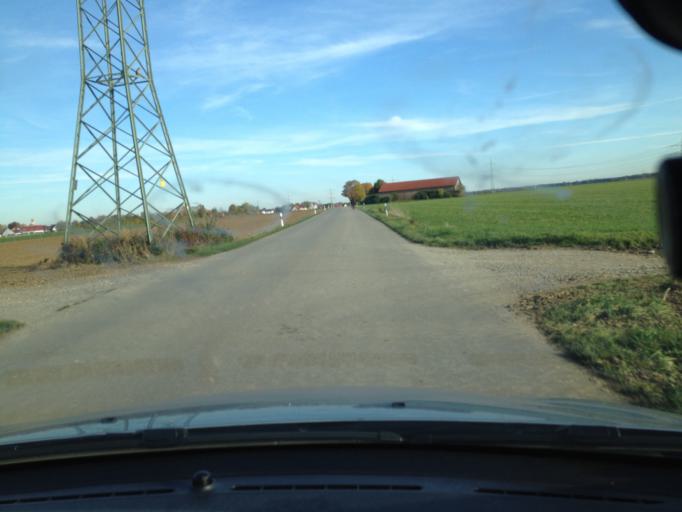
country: DE
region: Bavaria
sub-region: Swabia
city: Oberottmarshausen
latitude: 48.2358
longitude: 10.8422
